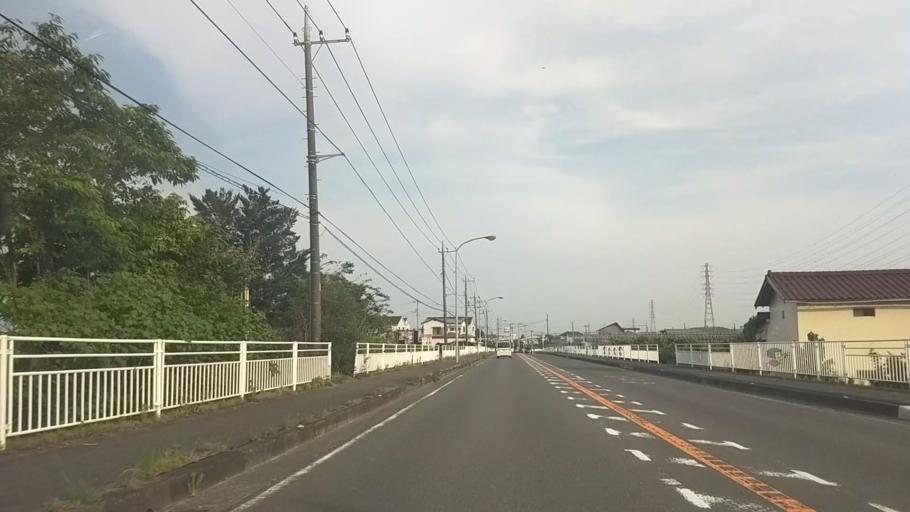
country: JP
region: Kanagawa
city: Odawara
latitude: 35.3392
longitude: 139.1036
